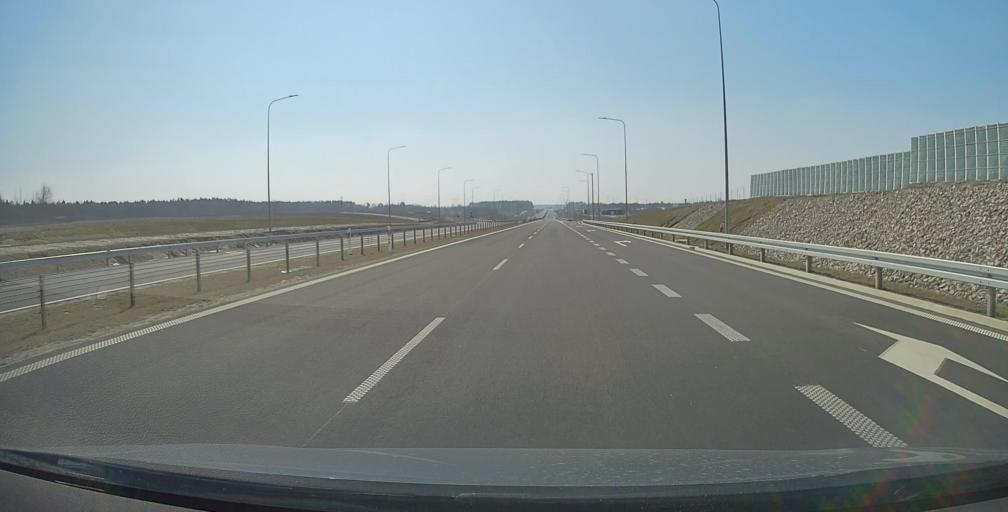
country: PL
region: Lublin Voivodeship
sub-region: Powiat janowski
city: Modliborzyce
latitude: 50.7857
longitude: 22.2916
